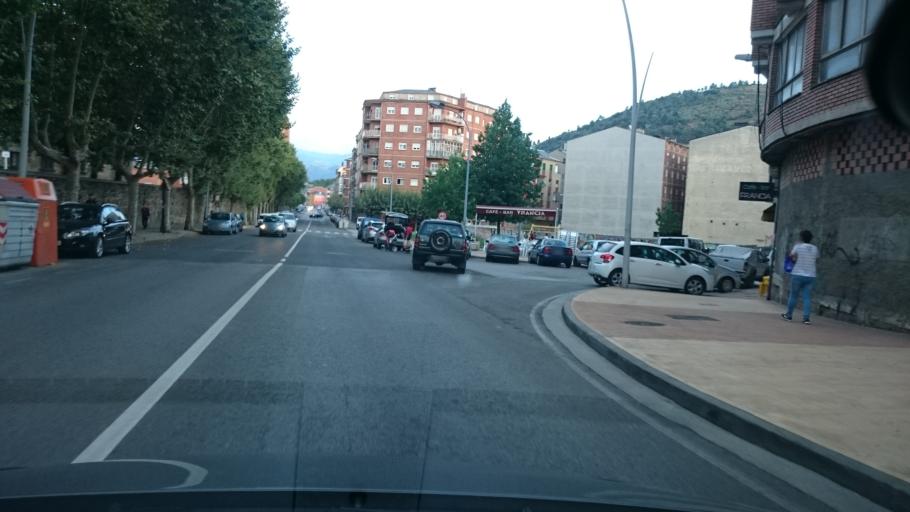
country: ES
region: Castille and Leon
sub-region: Provincia de Leon
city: Ponferrada
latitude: 42.5454
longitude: -6.6031
